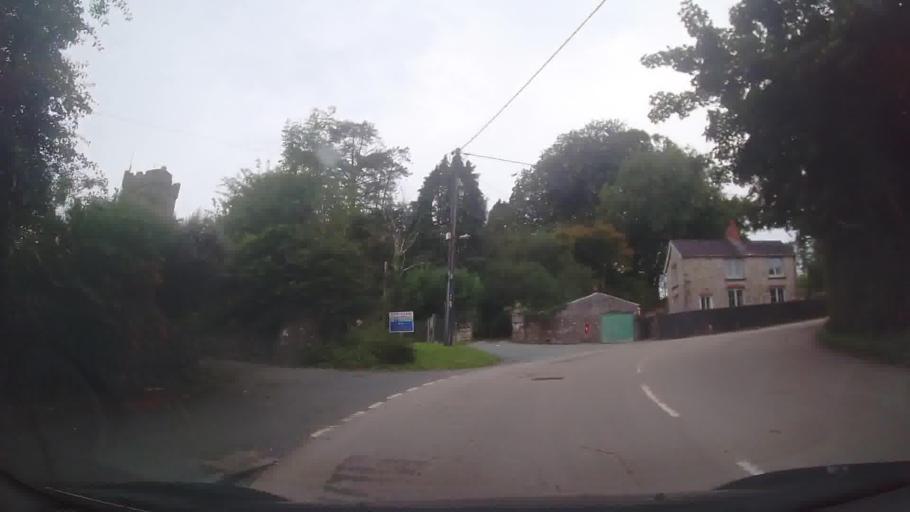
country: GB
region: Wales
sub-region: Pembrokeshire
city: Kilgetty
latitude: 51.7332
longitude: -4.7260
